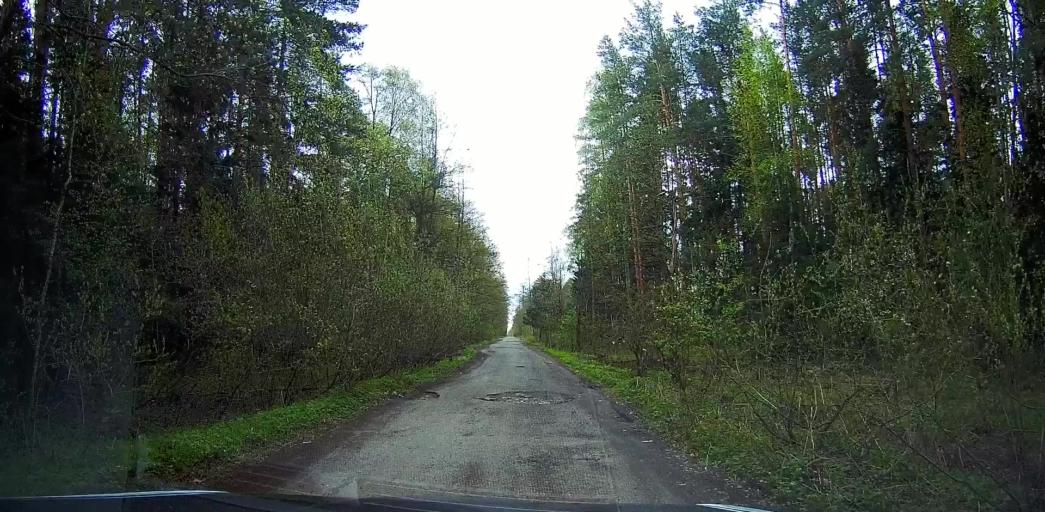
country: RU
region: Moskovskaya
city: Malyshevo
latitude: 55.5532
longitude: 38.3435
